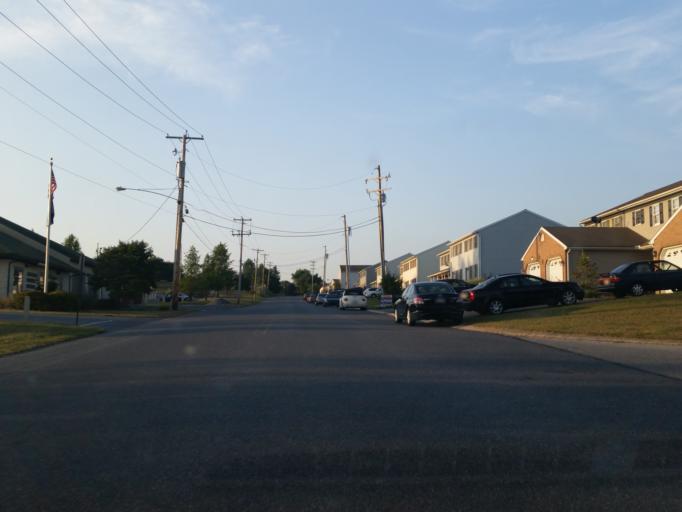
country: US
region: Pennsylvania
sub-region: Lebanon County
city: Jonestown
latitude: 40.4093
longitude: -76.4727
